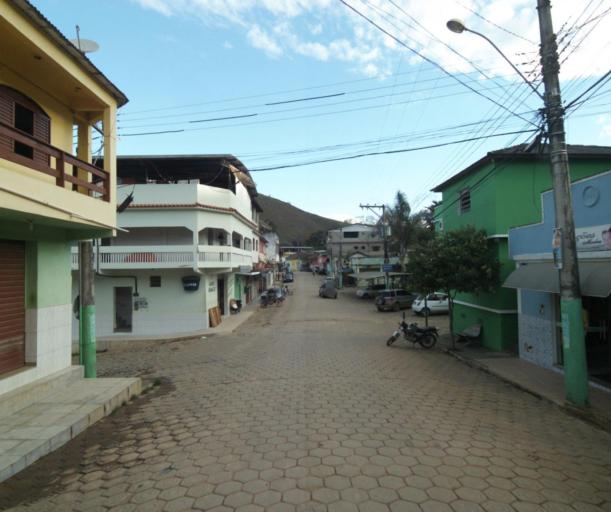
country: BR
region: Espirito Santo
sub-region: Guacui
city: Guacui
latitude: -20.6203
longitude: -41.6852
